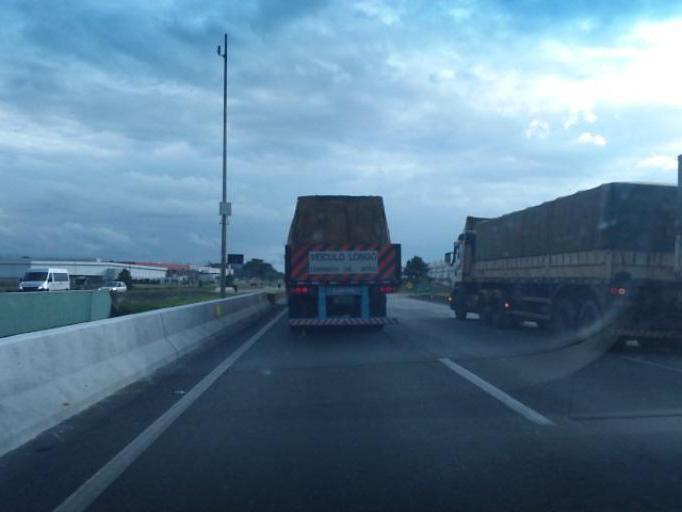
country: BR
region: Parana
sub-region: Sao Jose Dos Pinhais
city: Sao Jose dos Pinhais
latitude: -25.5119
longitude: -49.1283
